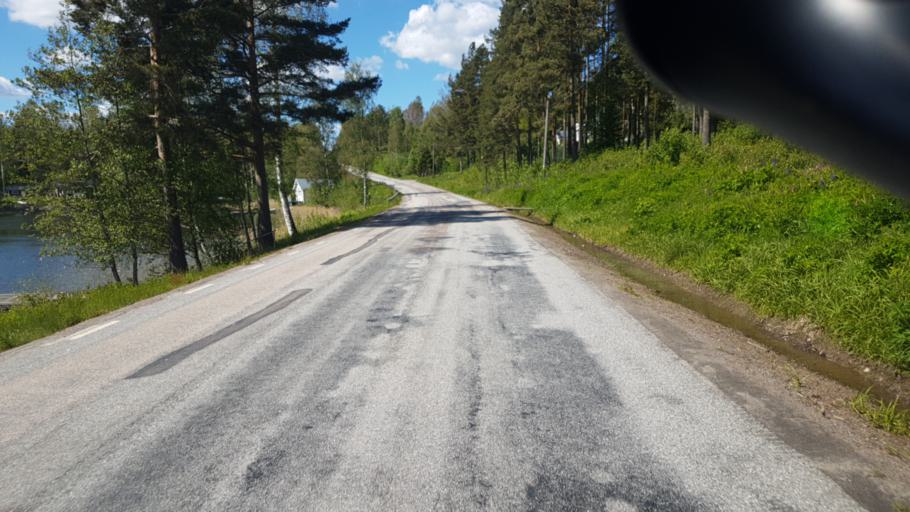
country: SE
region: Vaermland
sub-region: Arvika Kommun
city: Arvika
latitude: 59.6646
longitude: 12.6841
